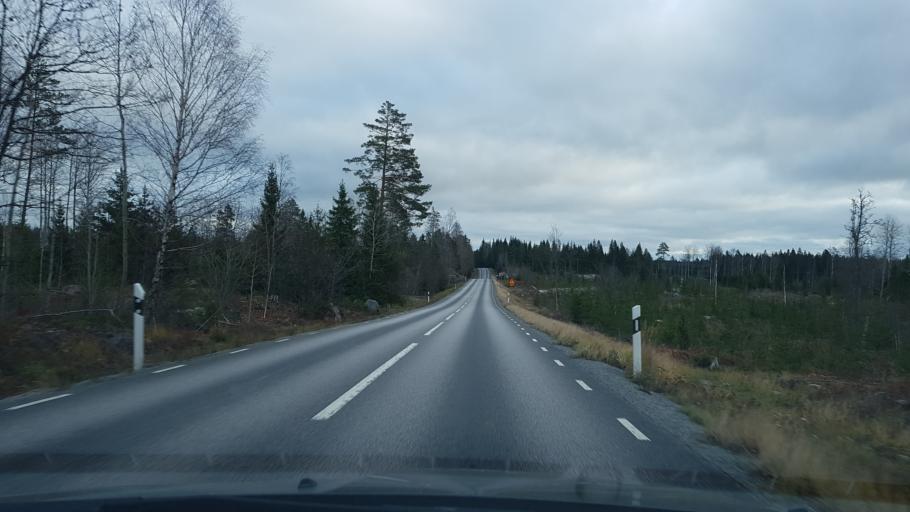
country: SE
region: Stockholm
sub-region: Norrtalje Kommun
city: Skanninge
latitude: 60.0337
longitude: 18.4618
